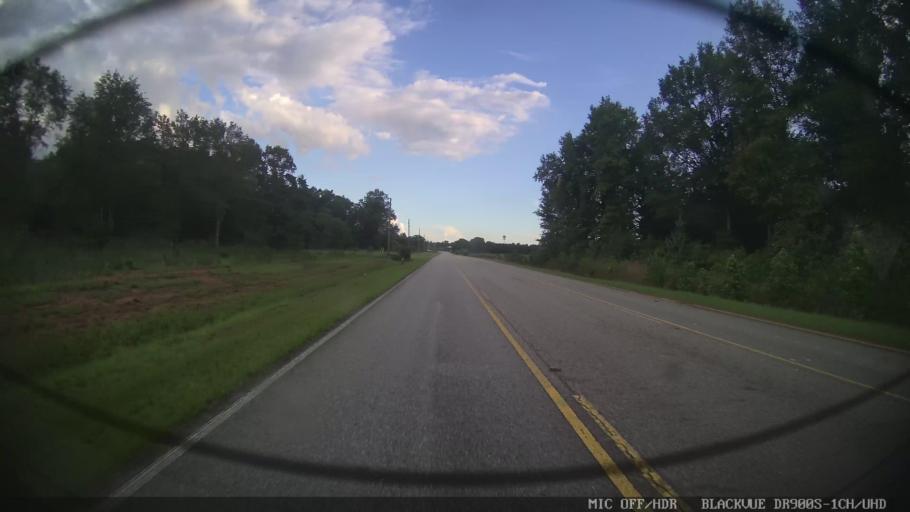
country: US
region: Georgia
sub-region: Peach County
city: Byron
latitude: 32.5990
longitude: -83.7399
